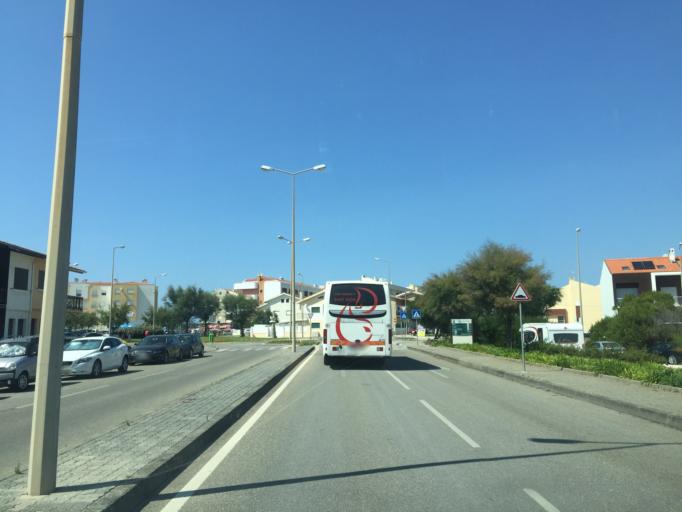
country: PT
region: Coimbra
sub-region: Mira
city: Mira
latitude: 40.3297
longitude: -8.8403
